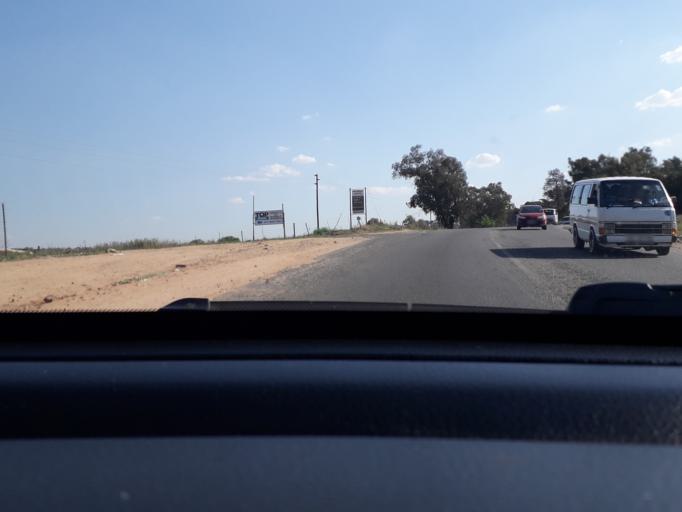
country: ZA
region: Gauteng
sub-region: City of Johannesburg Metropolitan Municipality
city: Midrand
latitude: -26.0342
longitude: 28.1111
